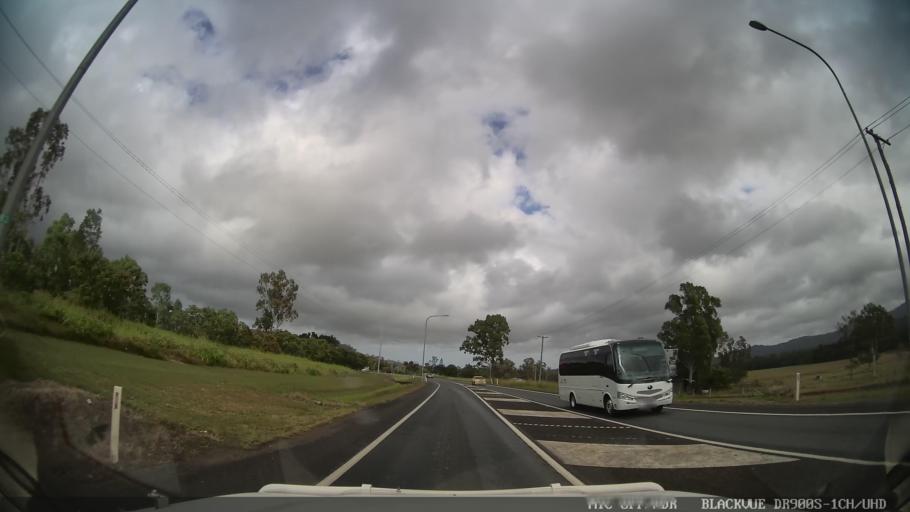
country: AU
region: Queensland
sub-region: Whitsunday
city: Proserpine
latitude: -20.3097
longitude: 148.6584
